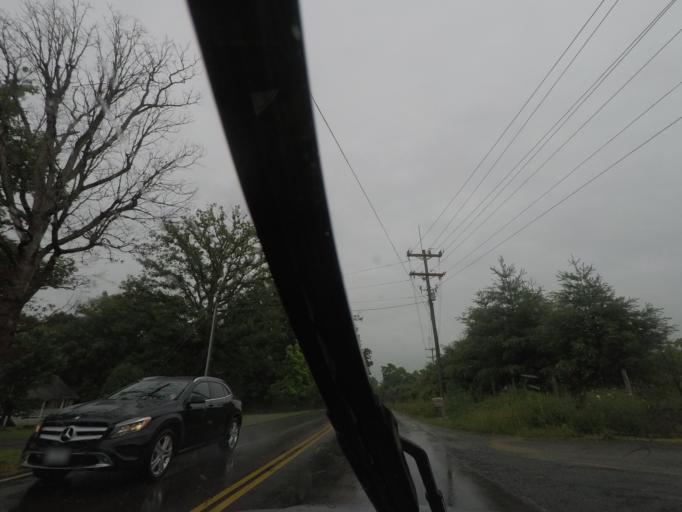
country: US
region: Virginia
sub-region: Culpeper County
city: Culpeper
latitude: 38.4770
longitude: -77.9558
